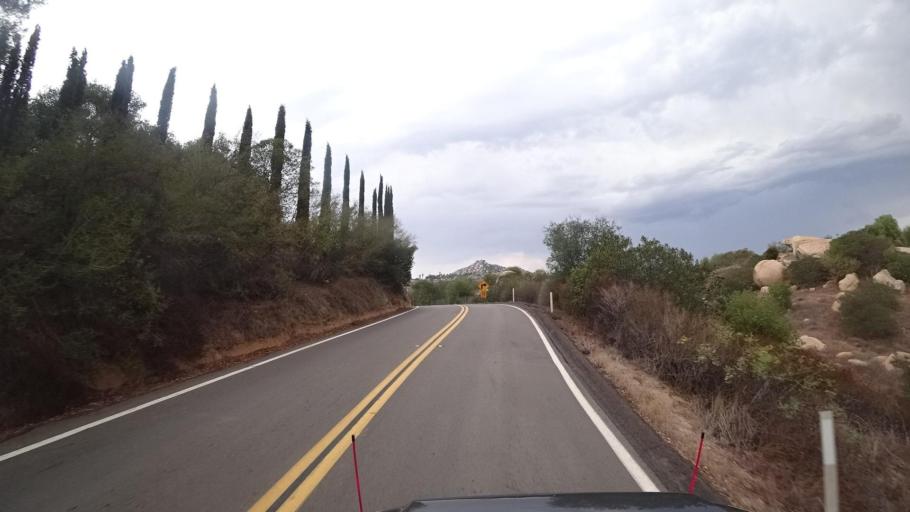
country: US
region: California
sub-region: San Diego County
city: San Pasqual
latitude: 33.0399
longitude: -116.9714
